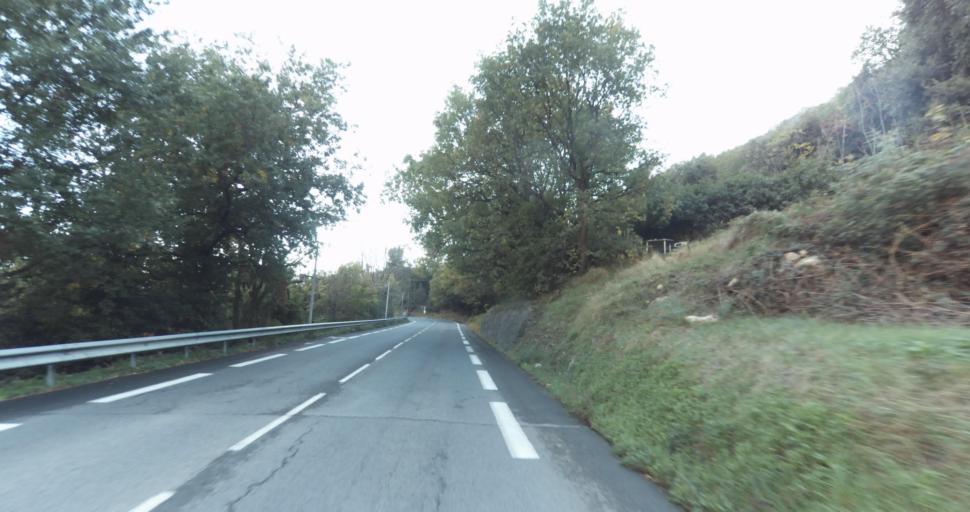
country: FR
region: Provence-Alpes-Cote d'Azur
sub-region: Departement des Alpes-Maritimes
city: Saint-Jeannet
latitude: 43.7479
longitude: 7.1301
